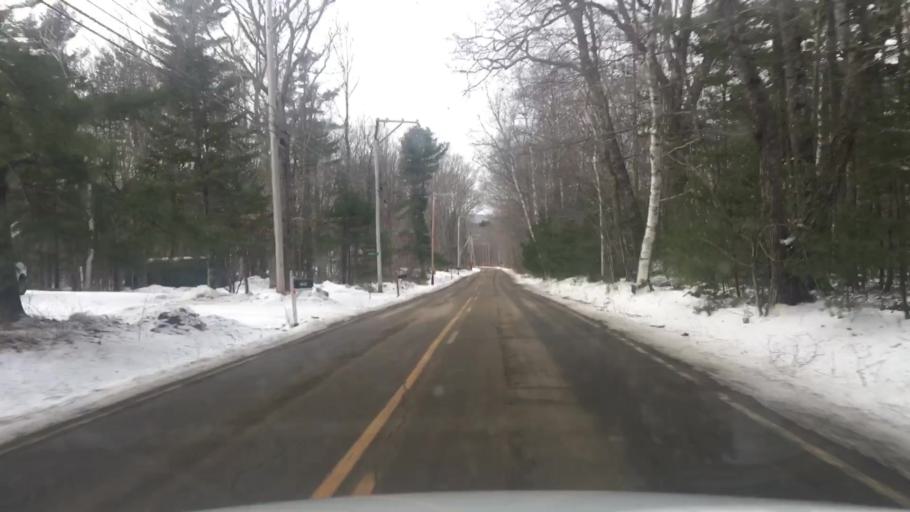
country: US
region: Maine
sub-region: Waldo County
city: Lincolnville
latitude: 44.2896
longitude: -69.0684
